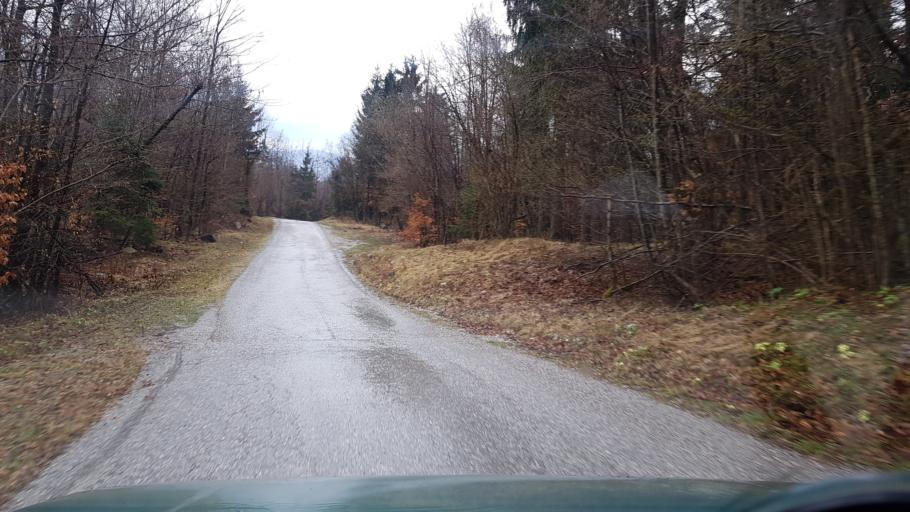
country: SI
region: Cerkno
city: Cerkno
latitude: 46.1339
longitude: 13.8739
